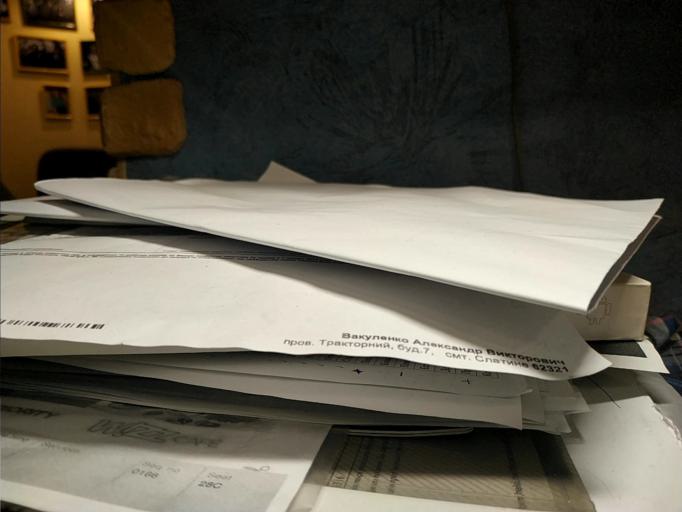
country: RU
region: Tverskaya
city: Zubtsov
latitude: 56.0956
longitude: 34.7144
